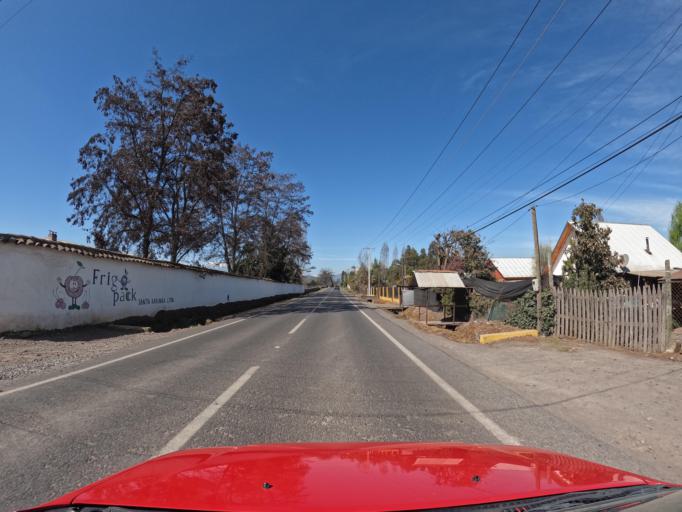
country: CL
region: Maule
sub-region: Provincia de Curico
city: Teno
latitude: -34.9676
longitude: -71.0303
